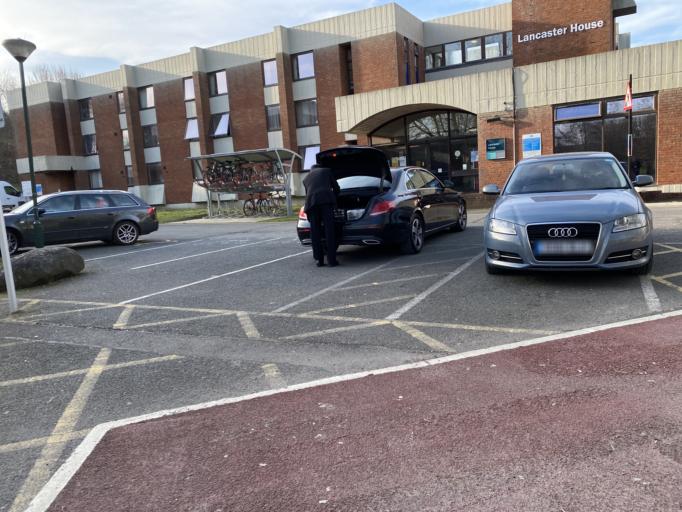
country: GB
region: England
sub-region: Brighton and Hove
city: Brighton
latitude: 50.8690
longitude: -0.0890
